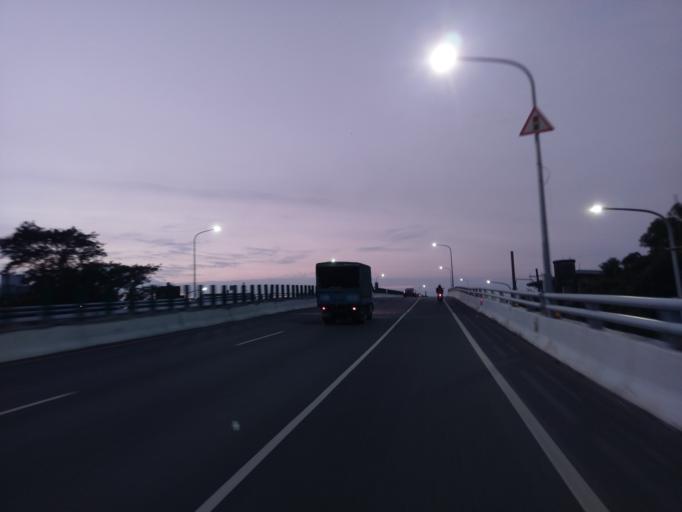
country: TW
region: Taiwan
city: Xinying
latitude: 23.1960
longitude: 120.3204
